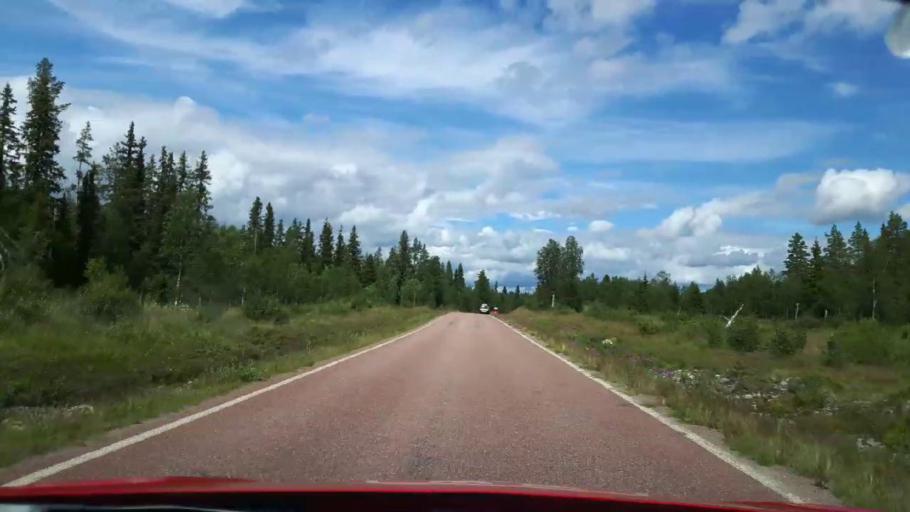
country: NO
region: Hedmark
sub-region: Trysil
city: Innbygda
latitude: 62.0057
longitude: 12.9758
